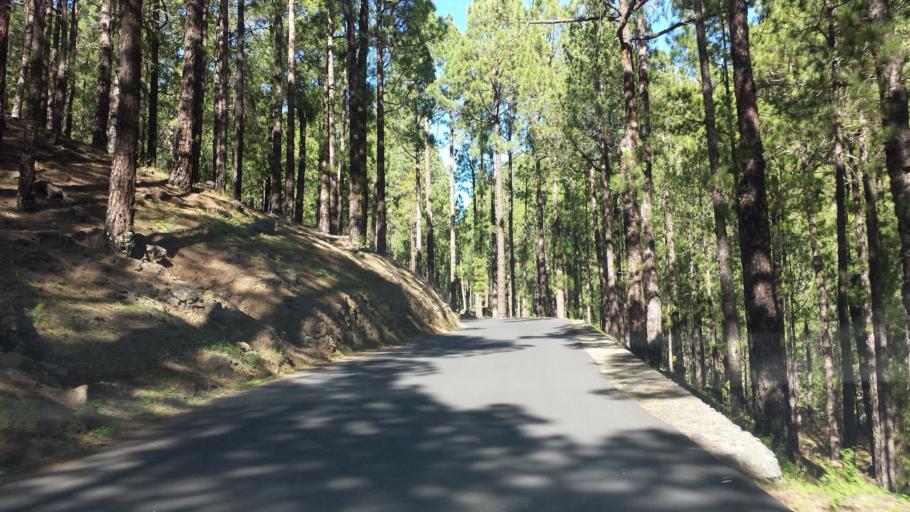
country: ES
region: Canary Islands
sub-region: Provincia de Santa Cruz de Tenerife
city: El Paso
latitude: 28.6907
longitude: -17.8512
